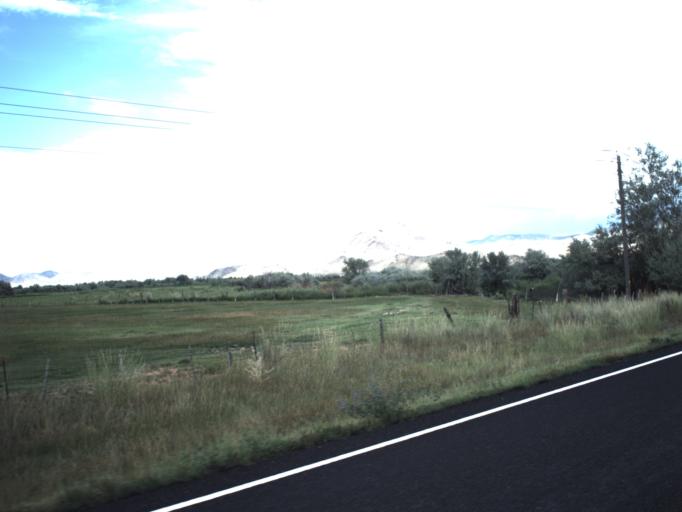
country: US
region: Utah
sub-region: Sevier County
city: Richfield
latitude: 38.7742
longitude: -112.0208
